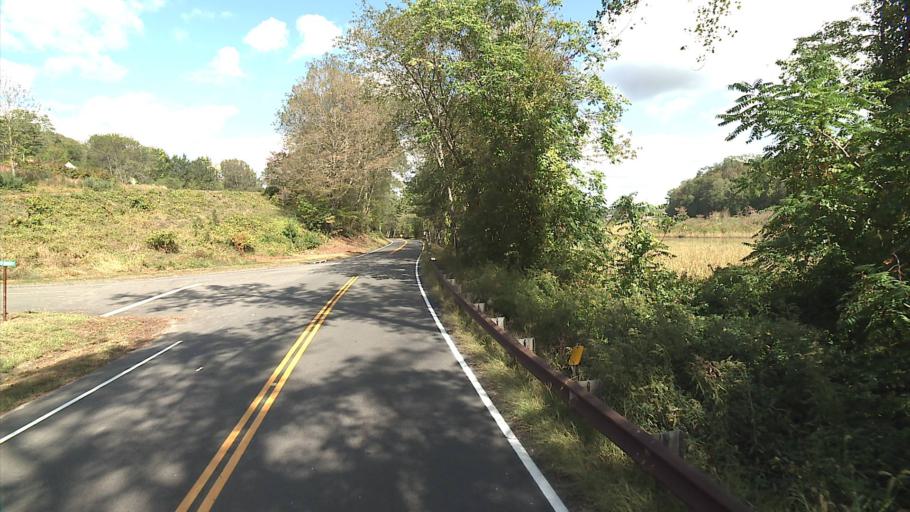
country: US
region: Connecticut
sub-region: Middlesex County
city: Chester Center
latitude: 41.4073
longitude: -72.4451
